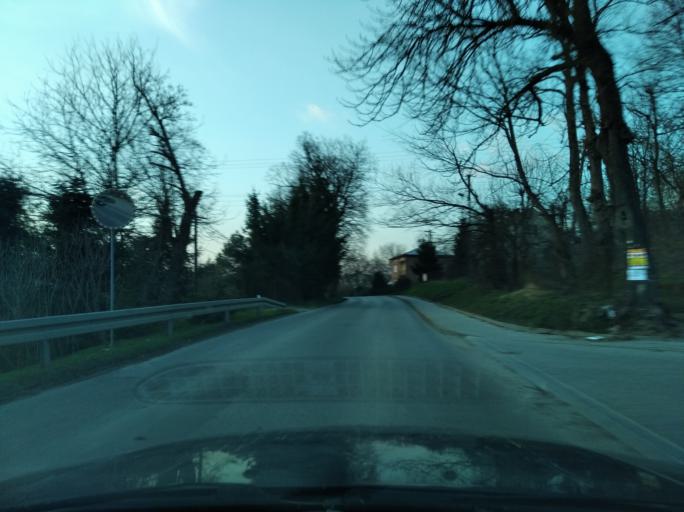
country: PL
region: Subcarpathian Voivodeship
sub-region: Powiat przeworski
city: Przeworsk
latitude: 50.0415
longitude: 22.5059
